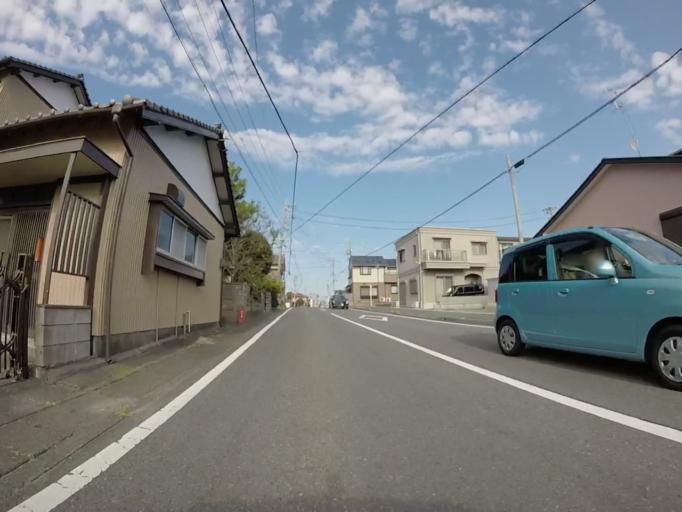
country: JP
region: Shizuoka
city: Sagara
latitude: 34.7340
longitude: 138.2247
